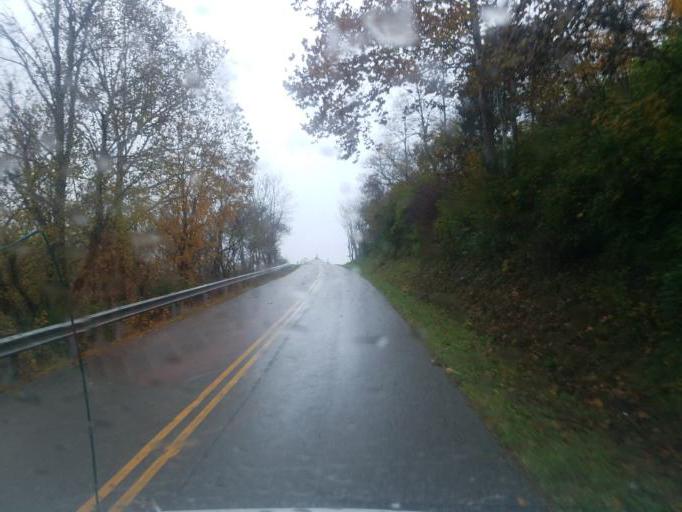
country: US
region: West Virginia
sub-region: Wood County
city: Vienna
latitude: 39.4250
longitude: -81.6177
